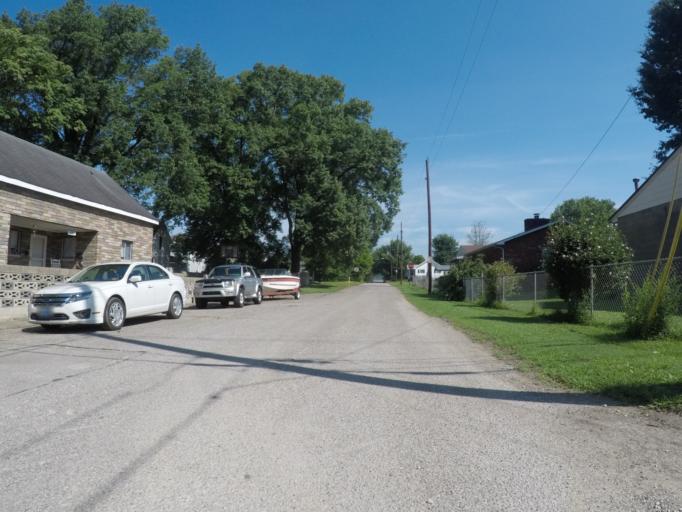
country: US
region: West Virginia
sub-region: Cabell County
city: Huntington
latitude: 38.4062
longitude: -82.4842
